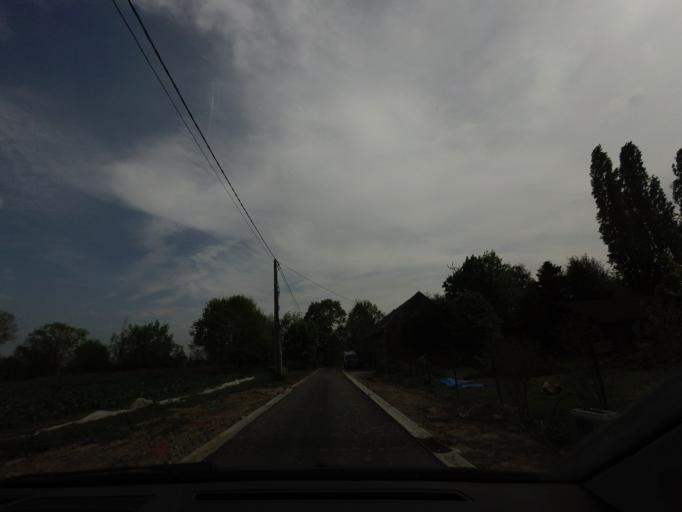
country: BE
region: Flanders
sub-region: Provincie Antwerpen
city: Kontich
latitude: 51.1128
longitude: 4.4611
